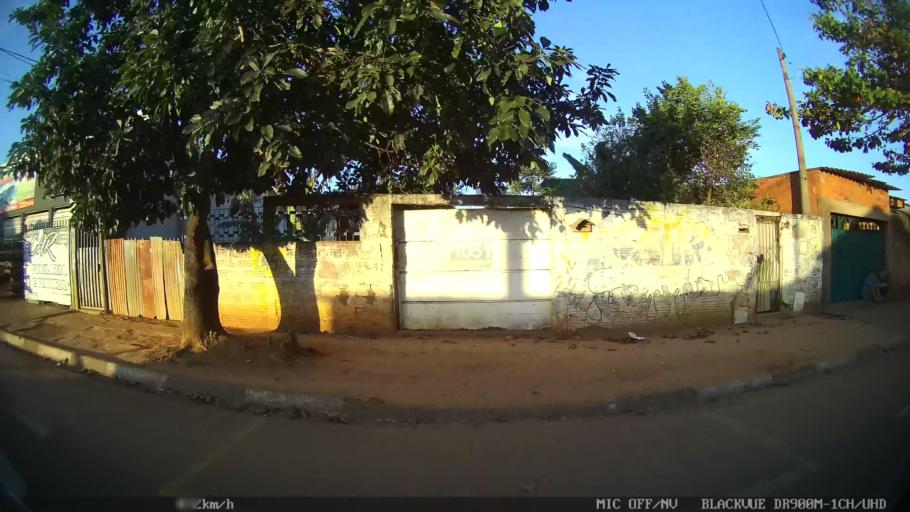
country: BR
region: Sao Paulo
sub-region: Franca
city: Franca
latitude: -20.5011
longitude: -47.3980
